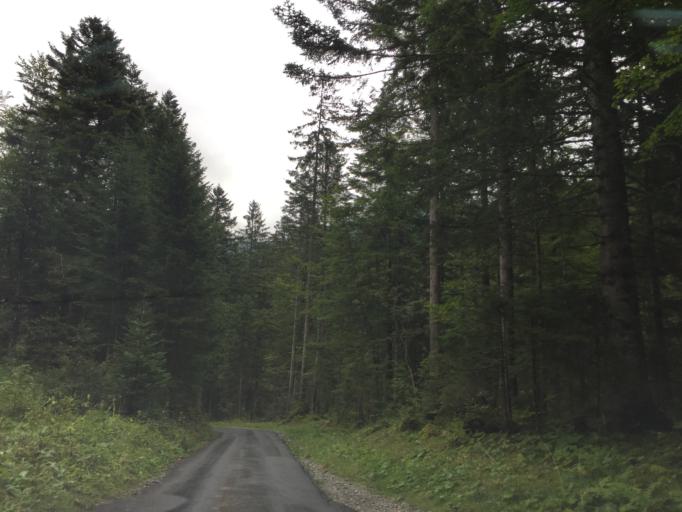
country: CH
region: Obwalden
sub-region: Obwalden
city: Sachseln
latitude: 46.7993
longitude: 8.2728
